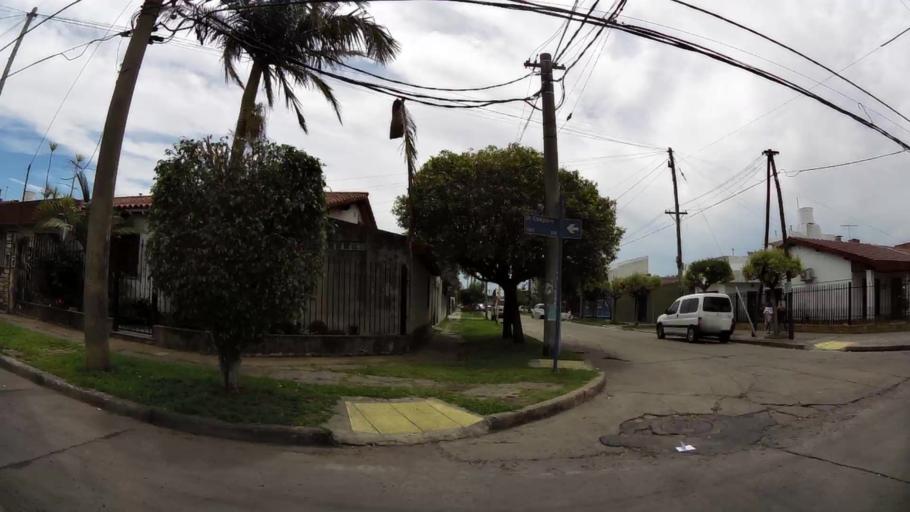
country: AR
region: Buenos Aires
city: San Justo
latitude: -34.6727
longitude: -58.5459
